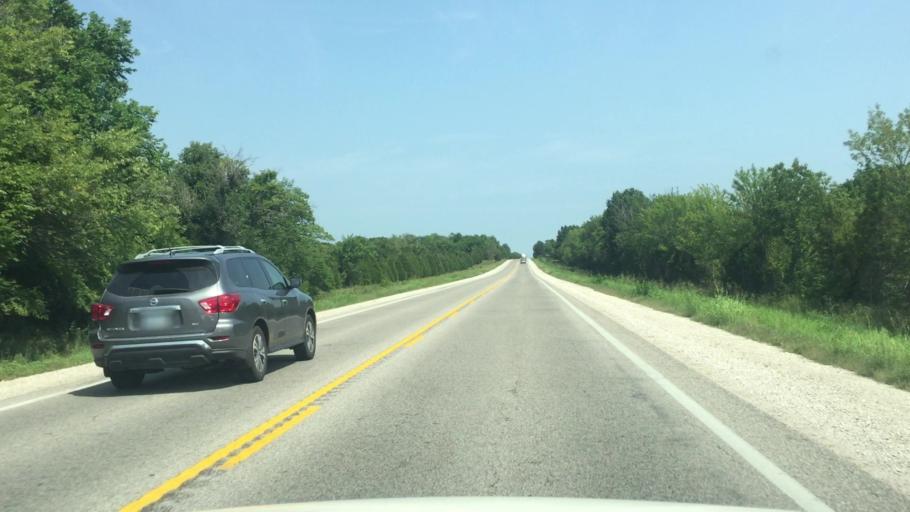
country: US
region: Kansas
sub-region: Montgomery County
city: Coffeyville
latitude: 37.1428
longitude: -95.5768
